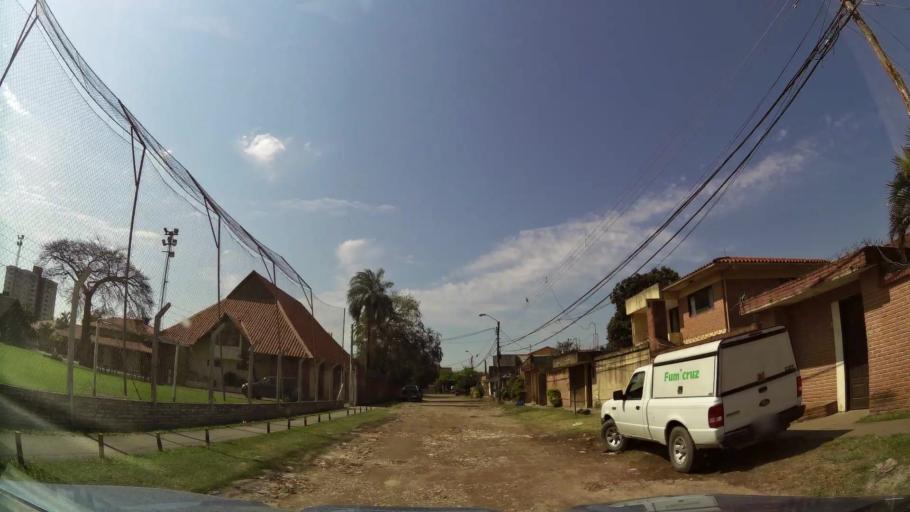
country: BO
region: Santa Cruz
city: Santa Cruz de la Sierra
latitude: -17.7484
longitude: -63.1653
